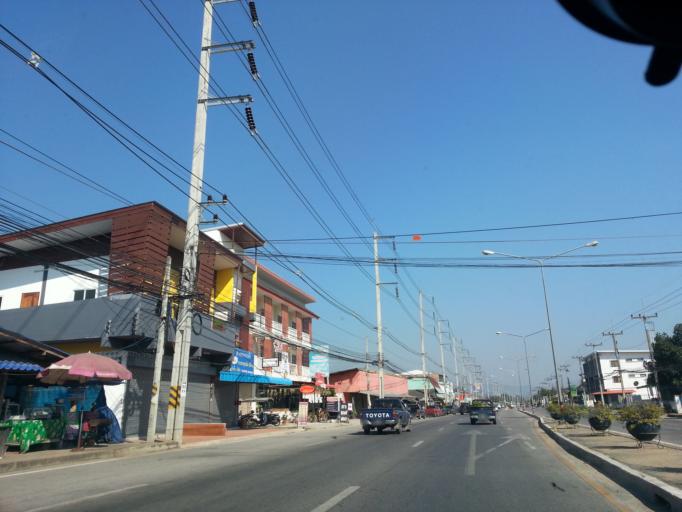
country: TH
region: Chiang Mai
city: Mae Taeng
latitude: 19.0981
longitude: 98.9356
